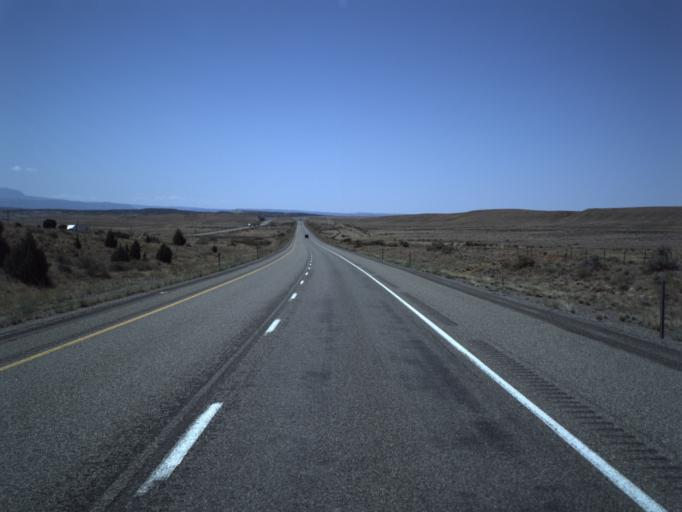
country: US
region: Colorado
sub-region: Mesa County
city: Loma
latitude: 39.1606
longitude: -109.1422
